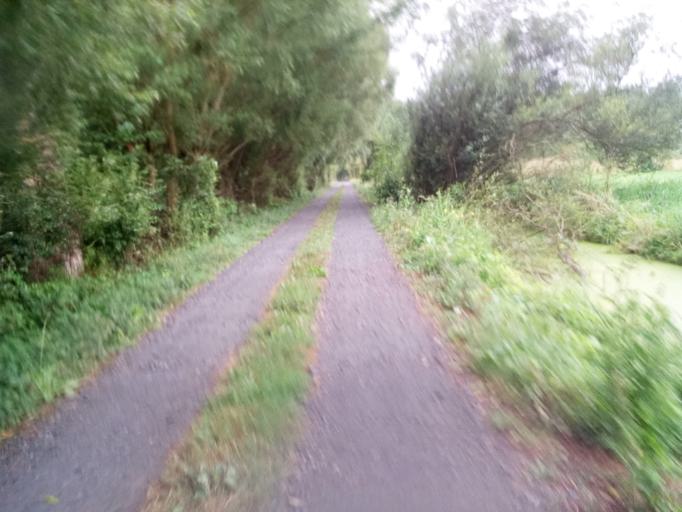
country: FR
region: Lower Normandy
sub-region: Departement du Calvados
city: Bavent
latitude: 49.2307
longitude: -0.1641
